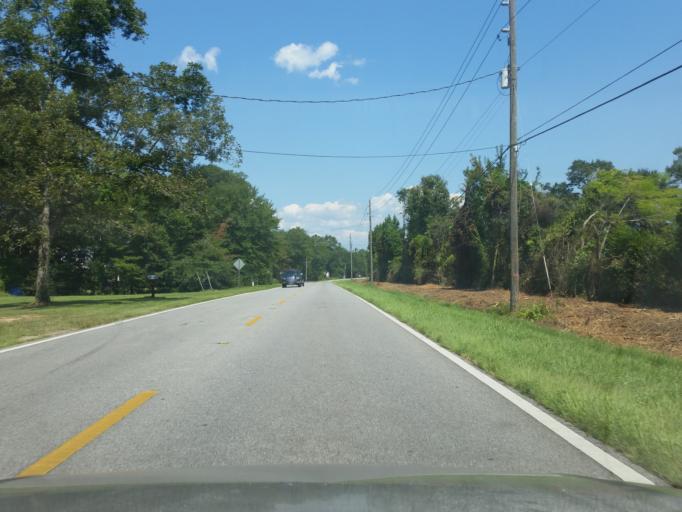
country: US
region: Florida
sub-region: Escambia County
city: Gonzalez
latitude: 30.5899
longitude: -87.3048
